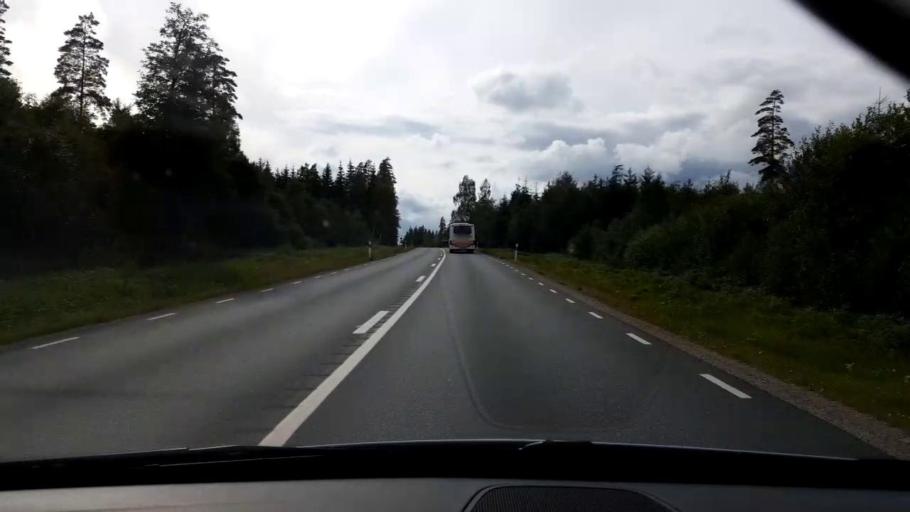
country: SE
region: Joenkoeping
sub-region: Savsjo Kommun
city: Saevsjoe
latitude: 57.3926
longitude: 14.7499
